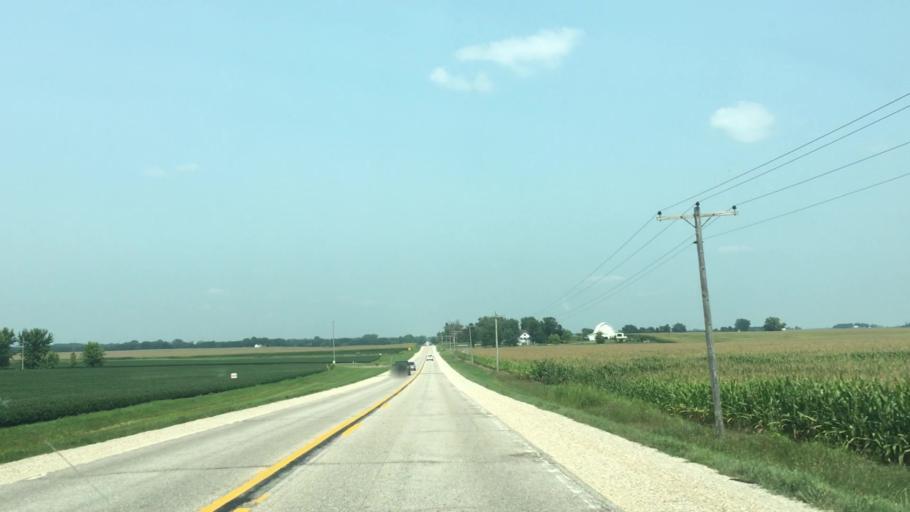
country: US
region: Iowa
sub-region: Benton County
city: Urbana
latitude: 42.3395
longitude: -91.8894
